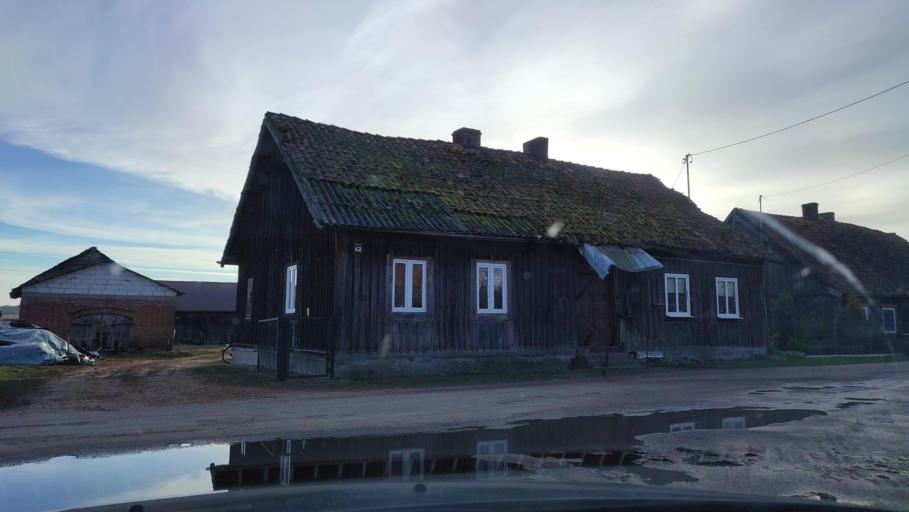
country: PL
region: Masovian Voivodeship
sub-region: Powiat przasnyski
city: Chorzele
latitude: 53.3404
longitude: 20.7543
